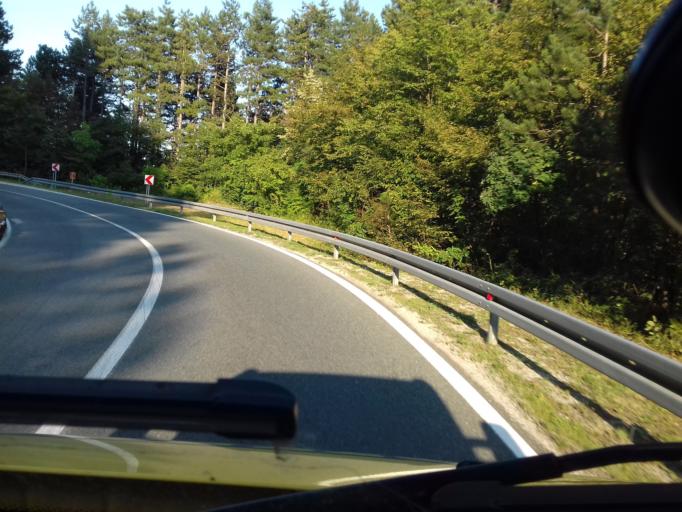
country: BA
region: Federation of Bosnia and Herzegovina
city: Ostrozac
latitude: 44.8997
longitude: 15.9299
